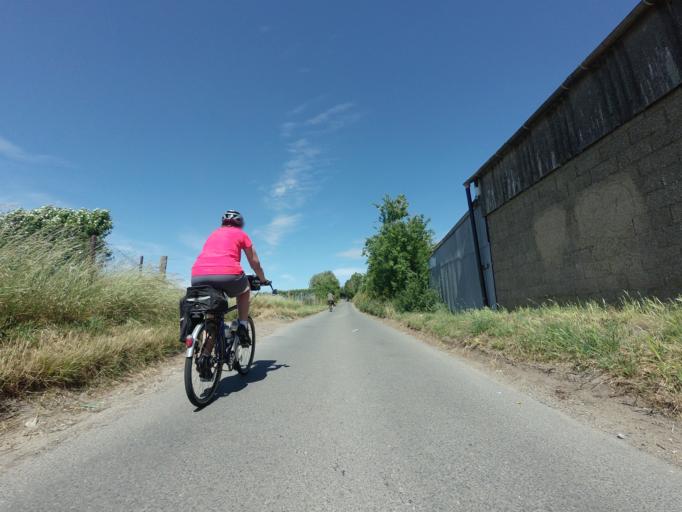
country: GB
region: England
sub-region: Kent
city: Strood
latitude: 51.4165
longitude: 0.5021
